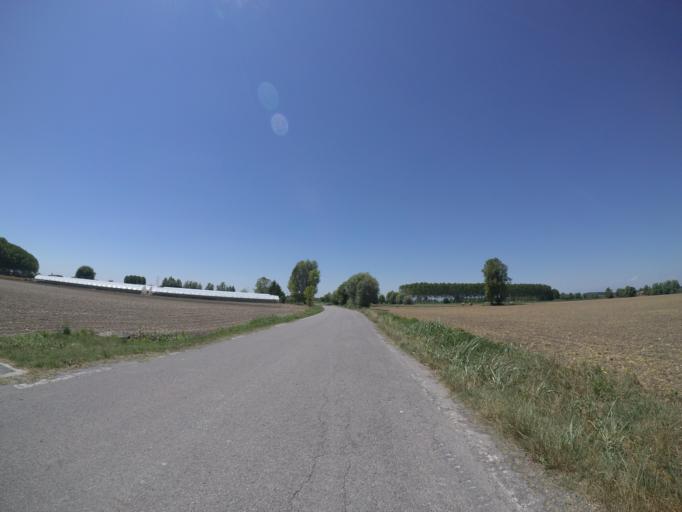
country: IT
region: Friuli Venezia Giulia
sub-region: Provincia di Udine
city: Teor
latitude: 45.8655
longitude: 13.0685
